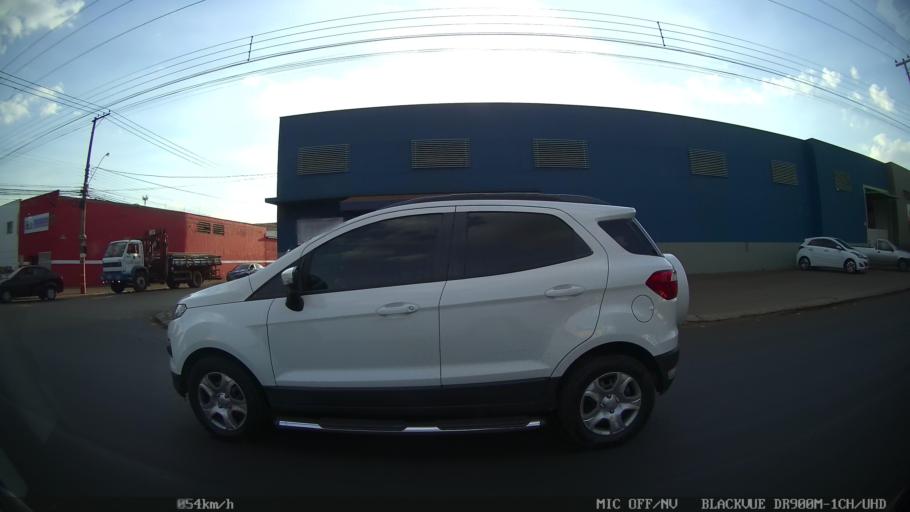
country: BR
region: Sao Paulo
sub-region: Ribeirao Preto
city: Ribeirao Preto
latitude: -21.1320
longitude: -47.7946
